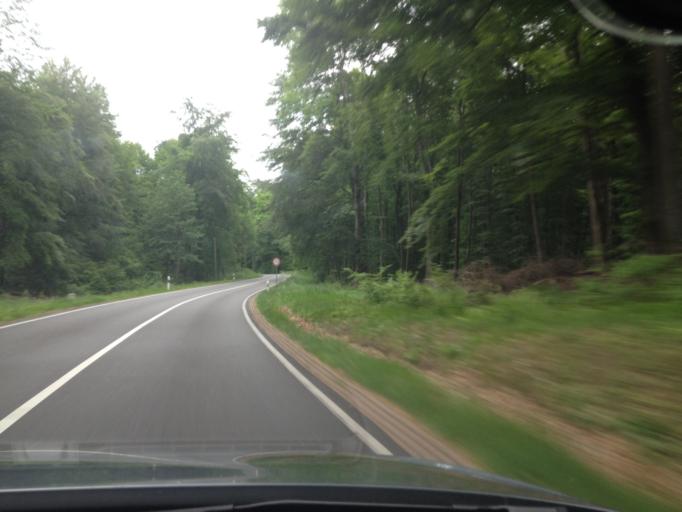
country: DE
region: Saarland
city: Neunkirchen
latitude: 49.3208
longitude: 7.1874
